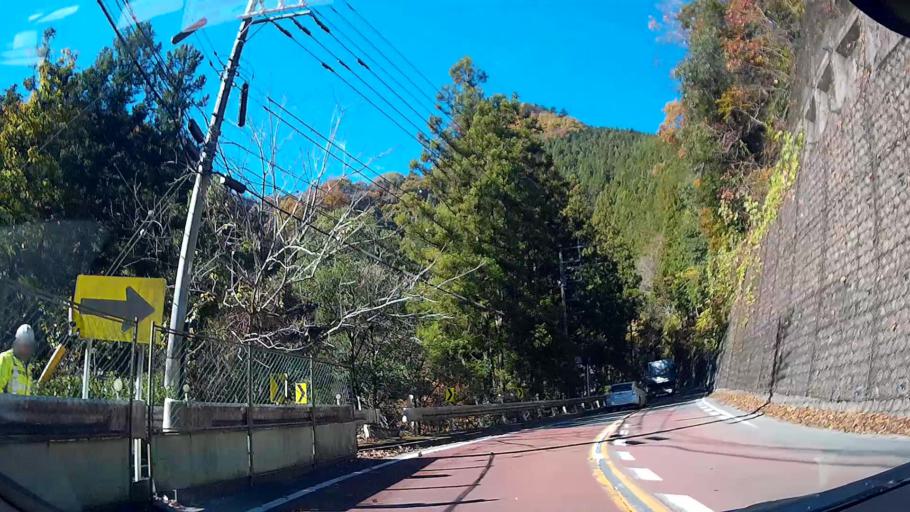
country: JP
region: Tokyo
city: Itsukaichi
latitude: 35.7246
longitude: 139.1466
